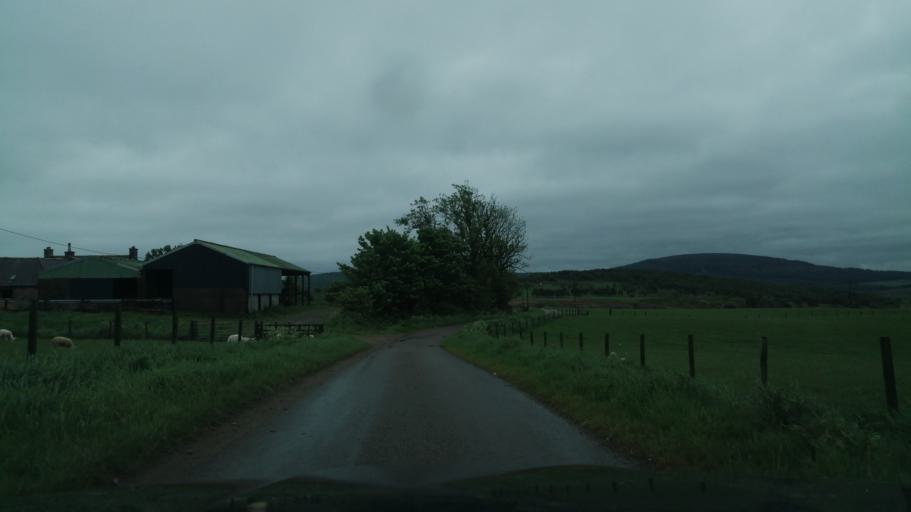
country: GB
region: Scotland
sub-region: Moray
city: Keith
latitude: 57.5726
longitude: -2.8612
